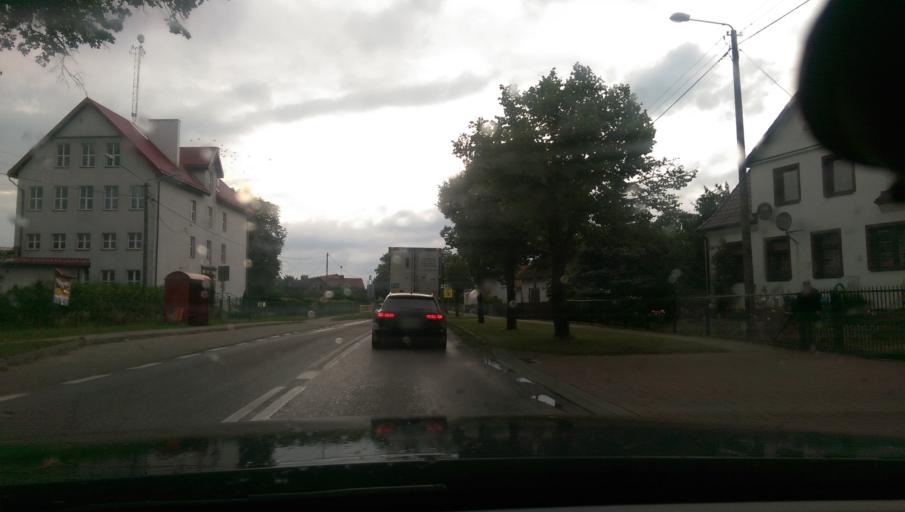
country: PL
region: Warmian-Masurian Voivodeship
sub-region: Powiat szczycienski
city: Swietajno
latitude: 53.5575
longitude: 21.1110
